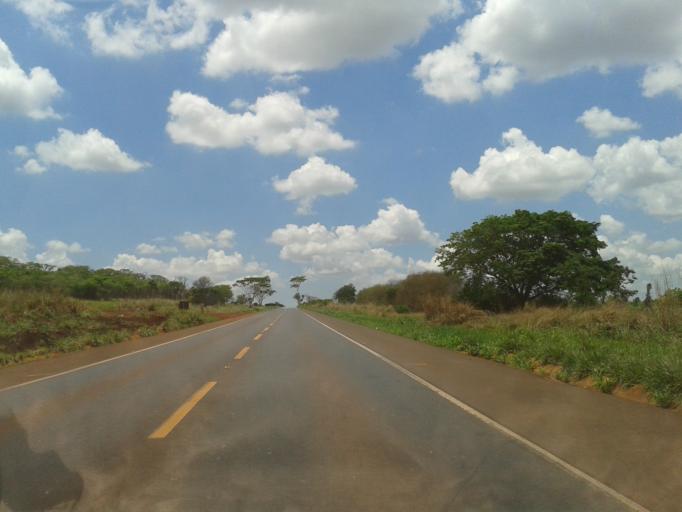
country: BR
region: Goias
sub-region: Itumbiara
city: Itumbiara
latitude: -18.3498
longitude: -49.3902
